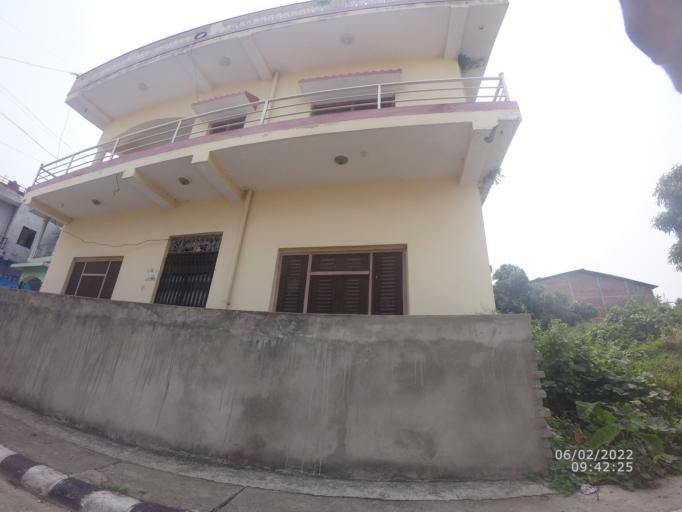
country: NP
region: Western Region
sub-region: Lumbini Zone
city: Bhairahawa
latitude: 27.5021
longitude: 83.4512
